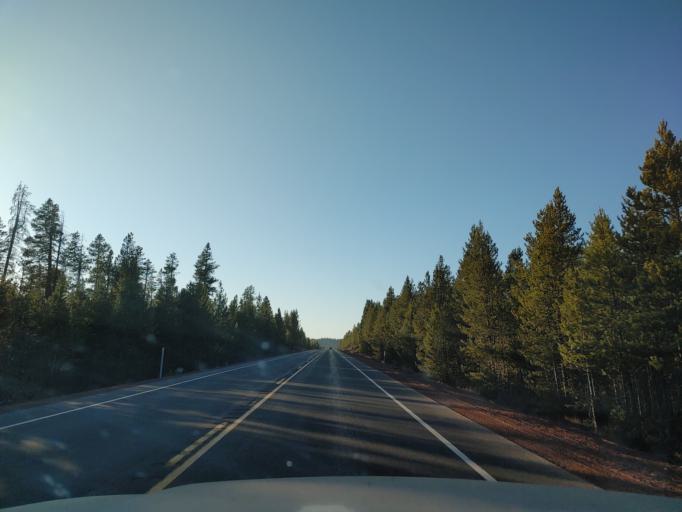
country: US
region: Oregon
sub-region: Deschutes County
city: La Pine
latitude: 43.4227
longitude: -121.8437
